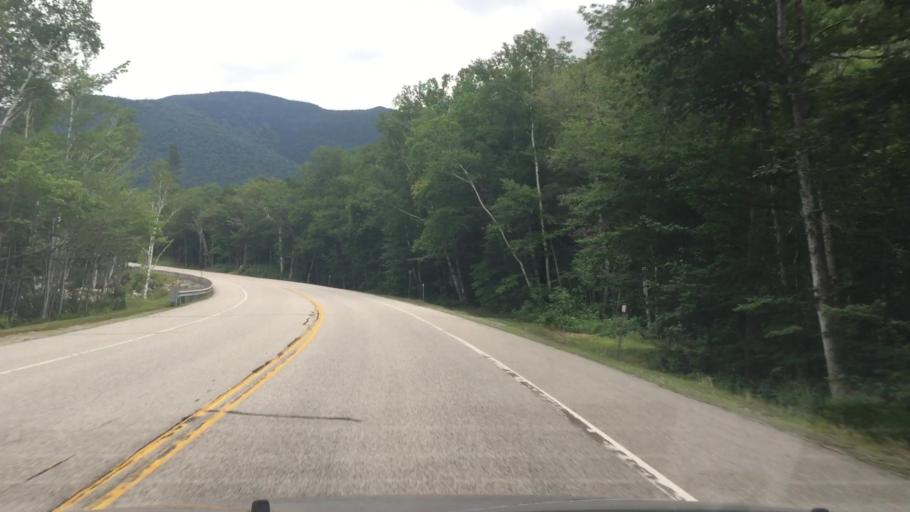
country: US
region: New Hampshire
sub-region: Grafton County
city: Deerfield
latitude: 44.1673
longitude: -71.3782
